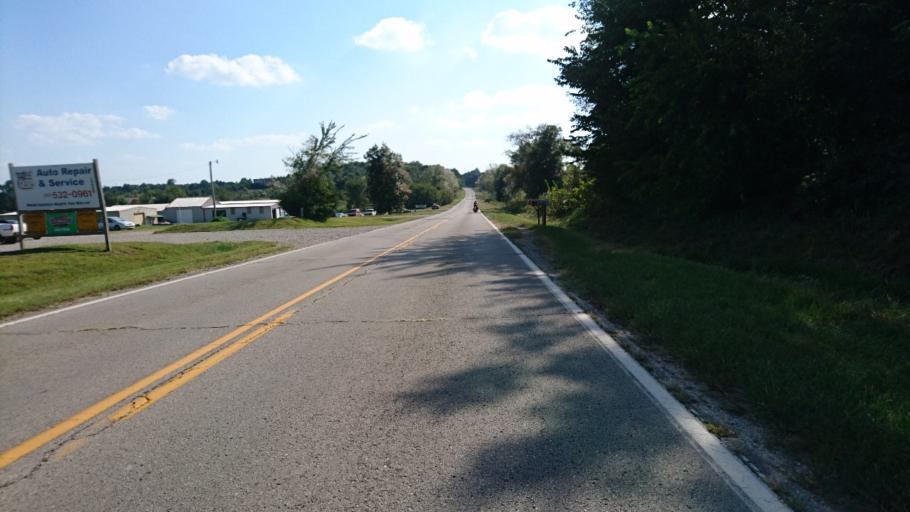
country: US
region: Missouri
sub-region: Laclede County
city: Lebanon
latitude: 37.6249
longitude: -92.6911
